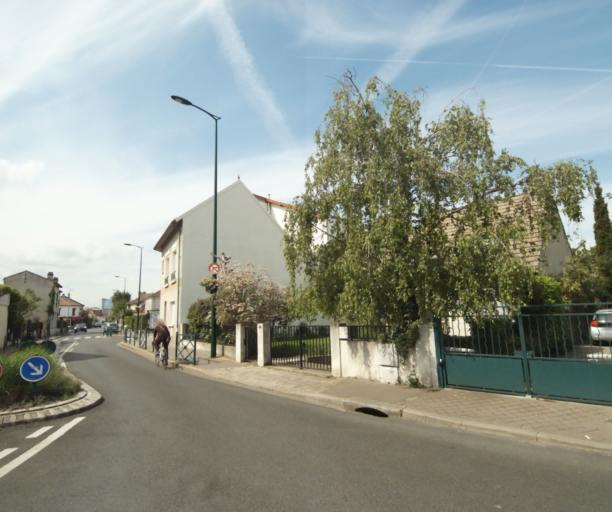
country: FR
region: Ile-de-France
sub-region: Departement des Hauts-de-Seine
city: Colombes
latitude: 48.9192
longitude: 2.2496
